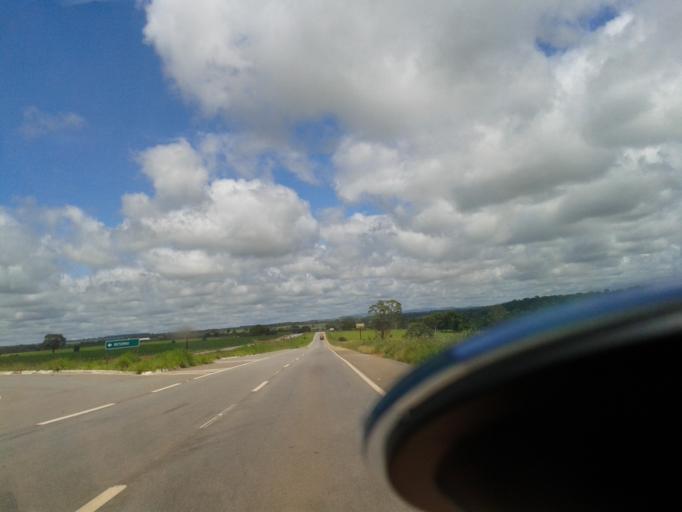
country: BR
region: Goias
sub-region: Itaberai
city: Itaberai
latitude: -16.1121
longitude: -49.6734
